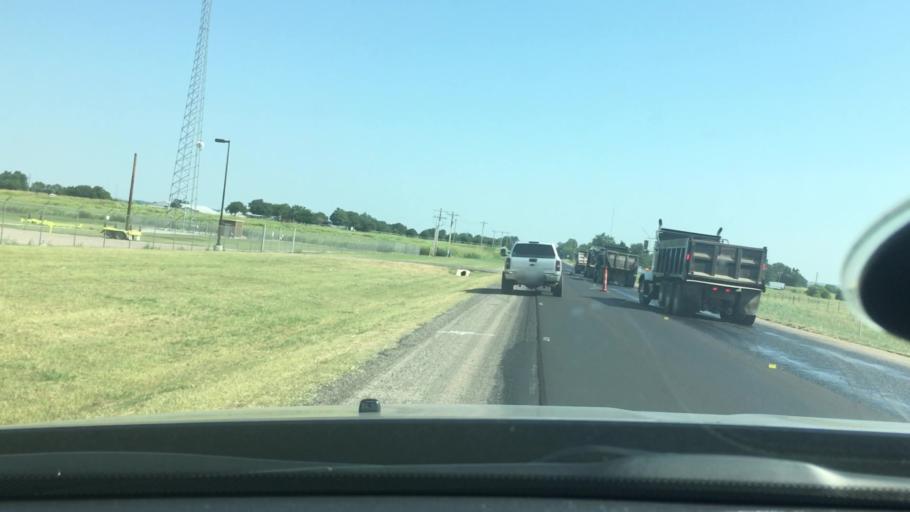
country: US
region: Oklahoma
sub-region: Garvin County
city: Lindsay
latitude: 34.7994
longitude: -97.5983
